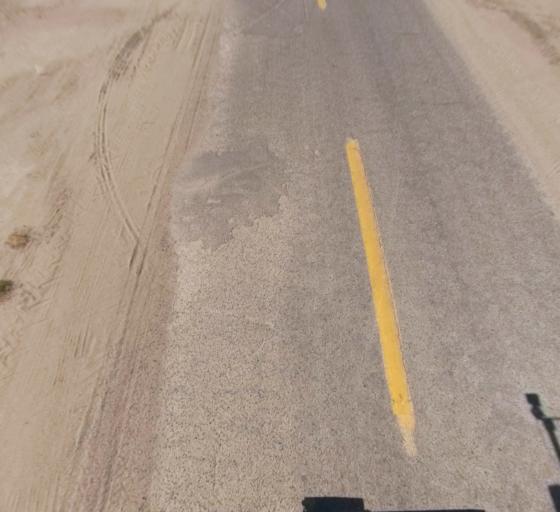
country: US
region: California
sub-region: Fresno County
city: Biola
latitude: 36.8403
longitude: -120.0282
